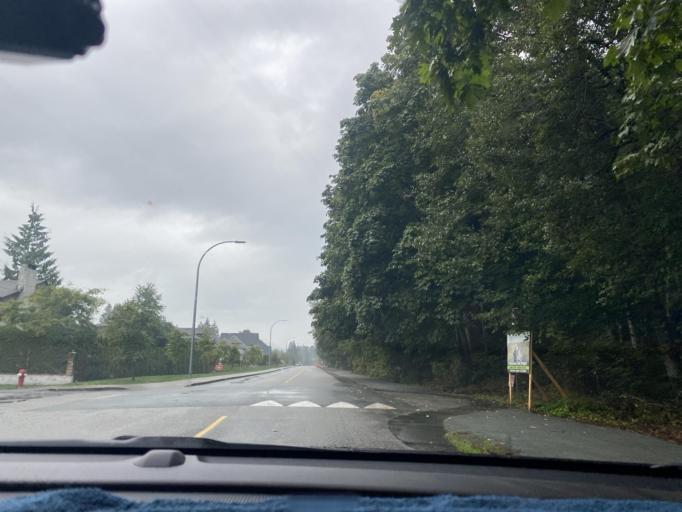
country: CA
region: British Columbia
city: Agassiz
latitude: 49.2912
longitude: -121.7775
